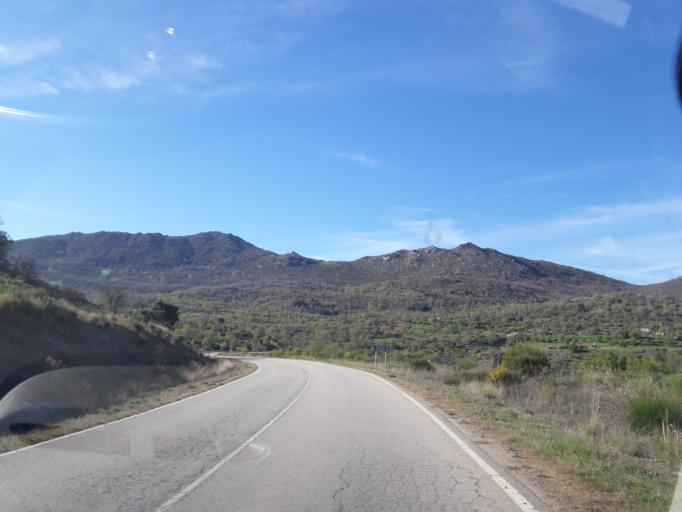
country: ES
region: Castille and Leon
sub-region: Provincia de Salamanca
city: Sanchotello
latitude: 40.4489
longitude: -5.7367
